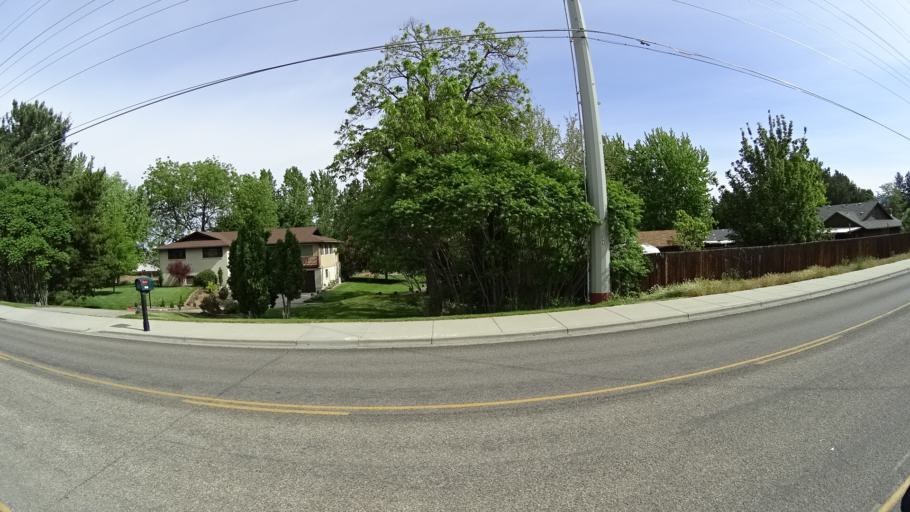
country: US
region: Idaho
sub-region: Ada County
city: Garden City
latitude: 43.5756
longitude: -116.3020
